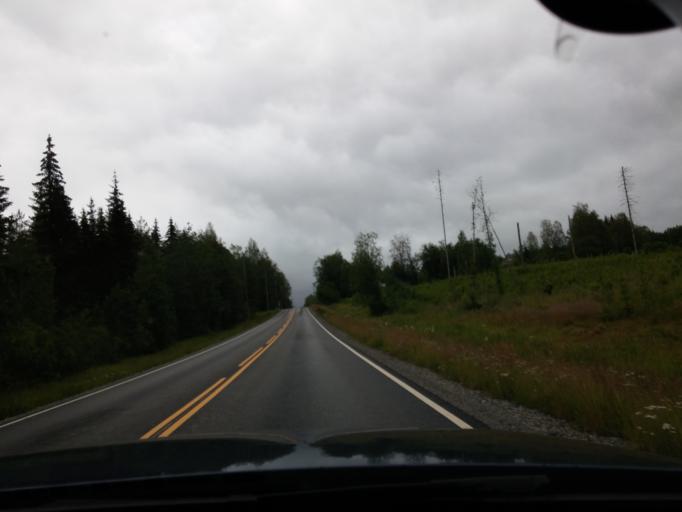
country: FI
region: Central Finland
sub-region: Saarijaervi-Viitasaari
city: Pylkoenmaeki
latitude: 62.6432
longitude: 24.9021
